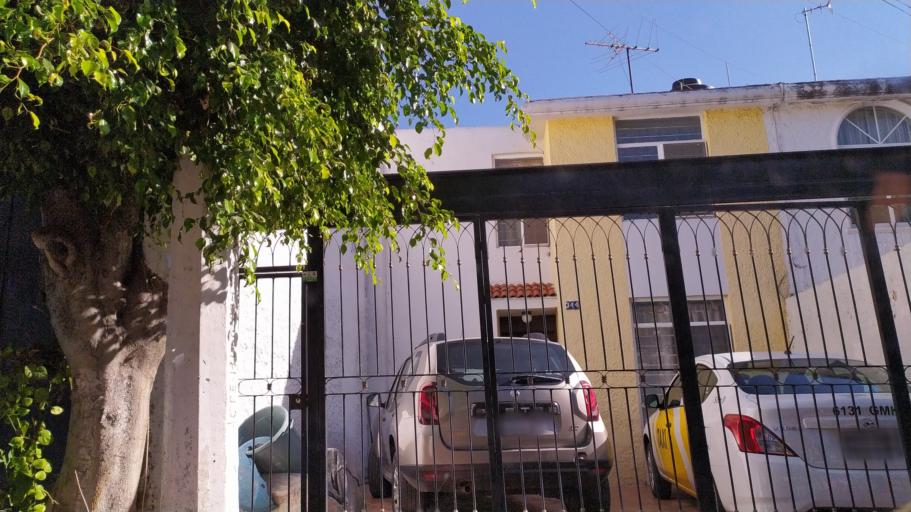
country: MX
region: Jalisco
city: Guadalajara
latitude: 20.6554
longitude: -103.4354
